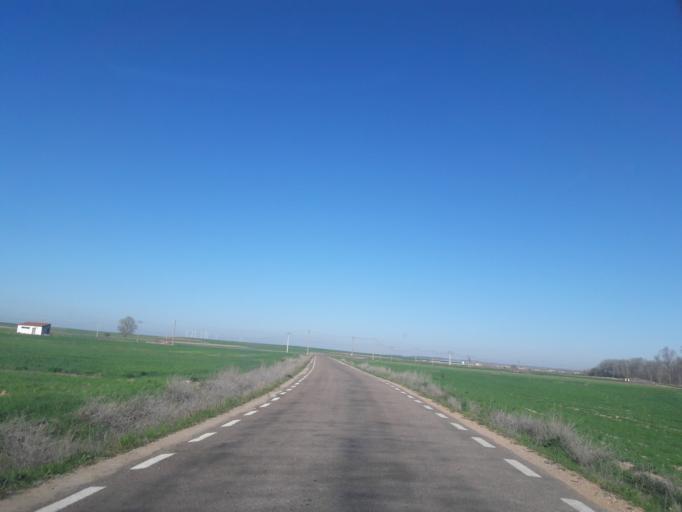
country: ES
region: Castille and Leon
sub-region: Provincia de Salamanca
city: Tordillos
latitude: 40.8599
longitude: -5.3606
